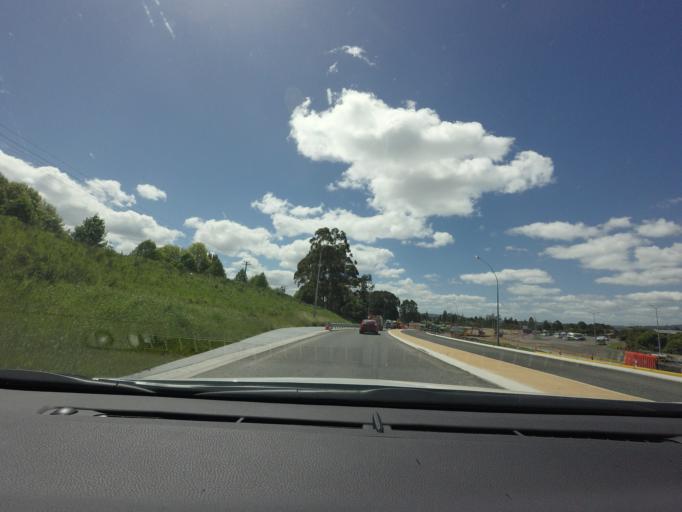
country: NZ
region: Bay of Plenty
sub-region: Rotorua District
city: Rotorua
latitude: -38.1673
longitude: 176.2454
